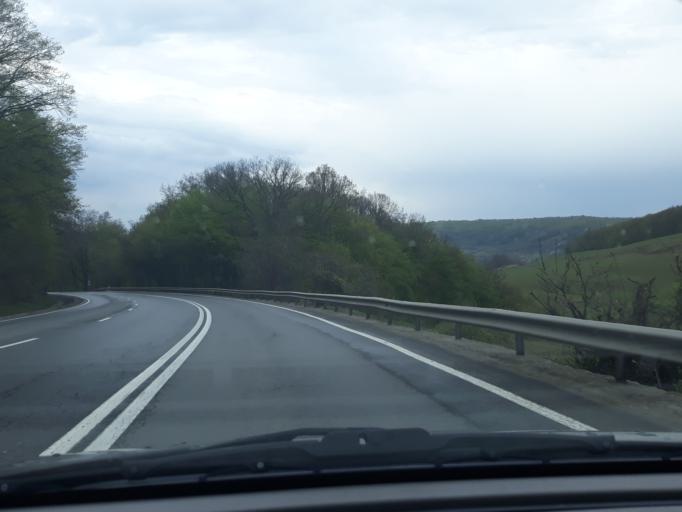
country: RO
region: Mures
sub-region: Comuna Balauseri
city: Balauseri
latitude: 46.4154
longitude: 24.6708
